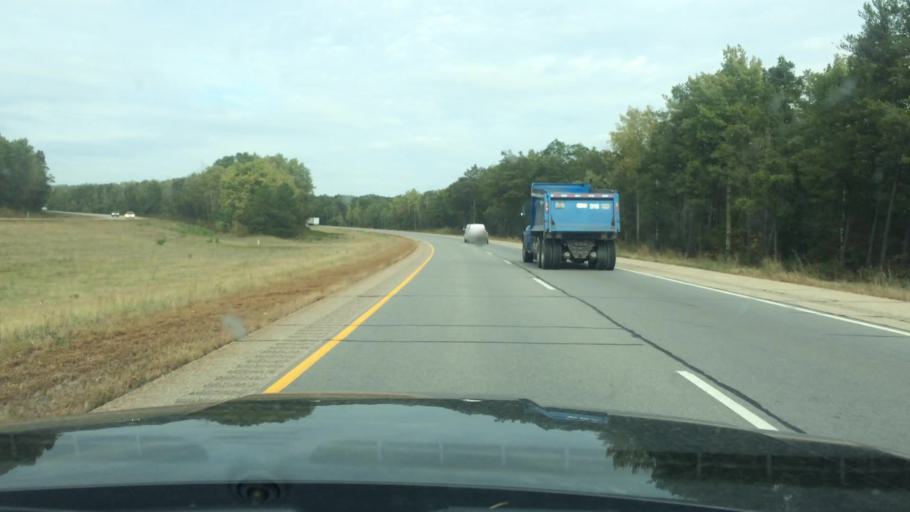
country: US
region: Wisconsin
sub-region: Marathon County
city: Mosinee
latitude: 44.6875
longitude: -89.6408
